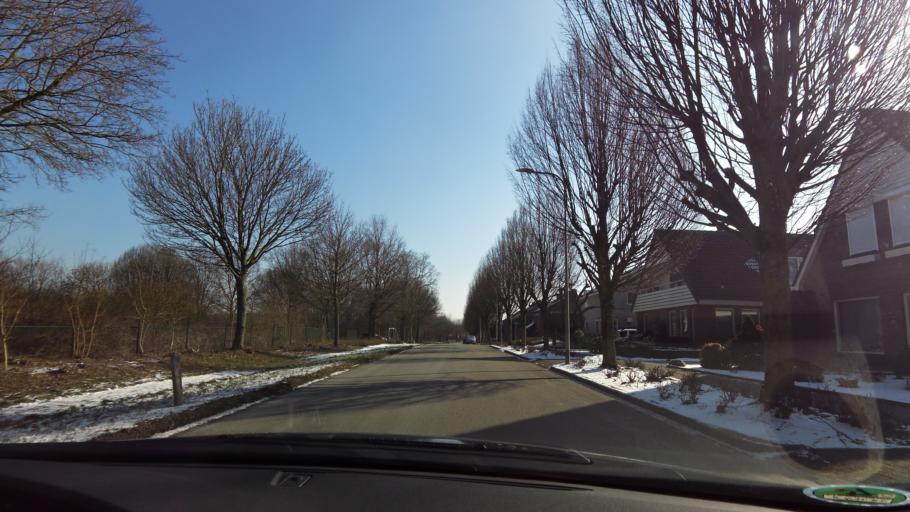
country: NL
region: Limburg
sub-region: Valkenburg aan de Geul
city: Berg
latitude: 50.8614
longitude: 5.7924
